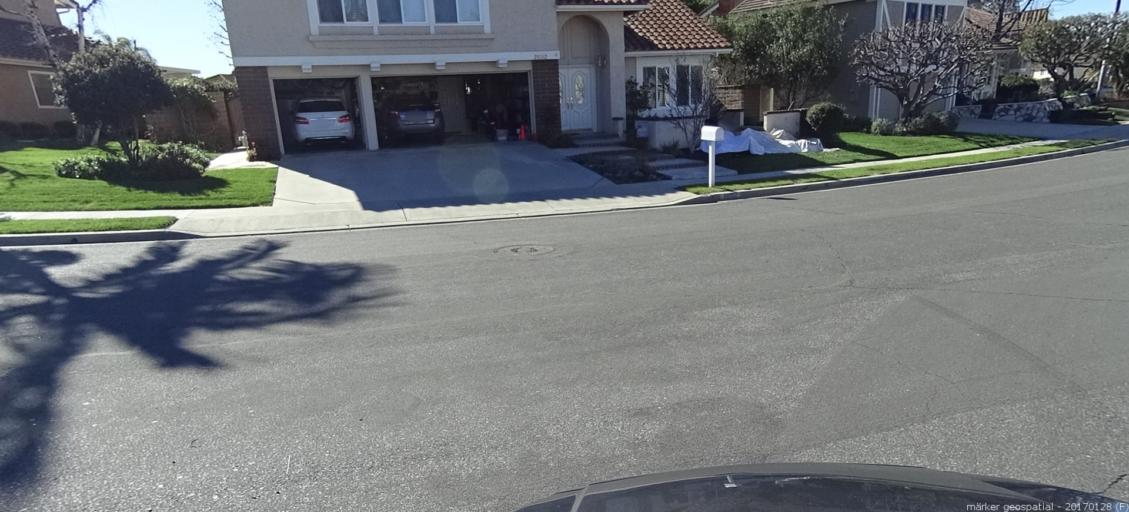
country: US
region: California
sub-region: Orange County
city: Lake Forest
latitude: 33.6570
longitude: -117.6947
